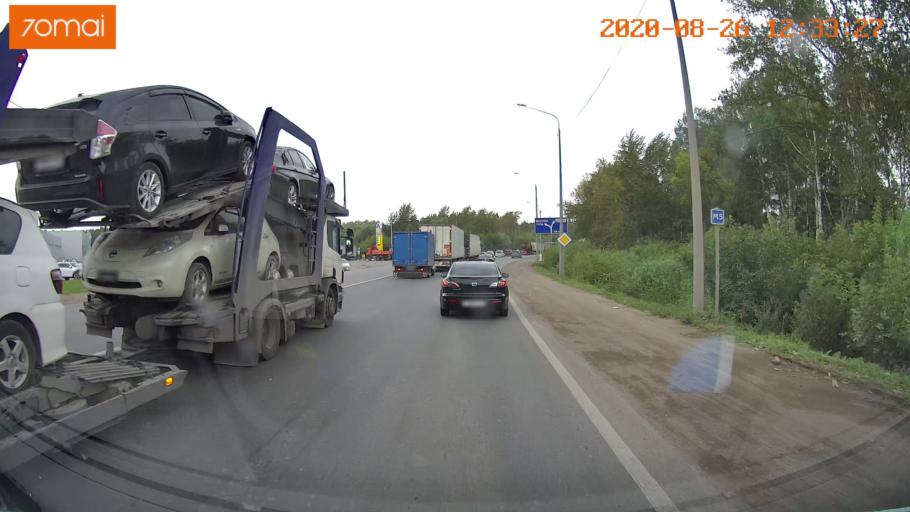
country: RU
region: Rjazan
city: Ryazan'
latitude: 54.5819
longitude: 39.7765
